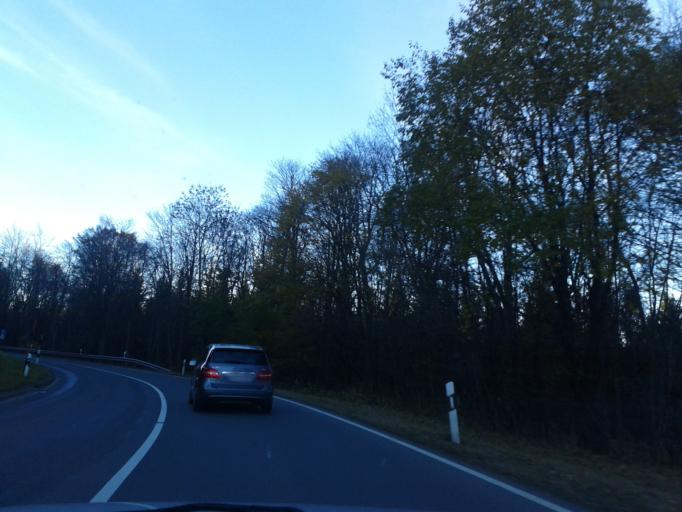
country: DE
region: North Rhine-Westphalia
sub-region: Regierungsbezirk Arnsberg
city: Winterberg
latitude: 51.1813
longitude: 8.4984
